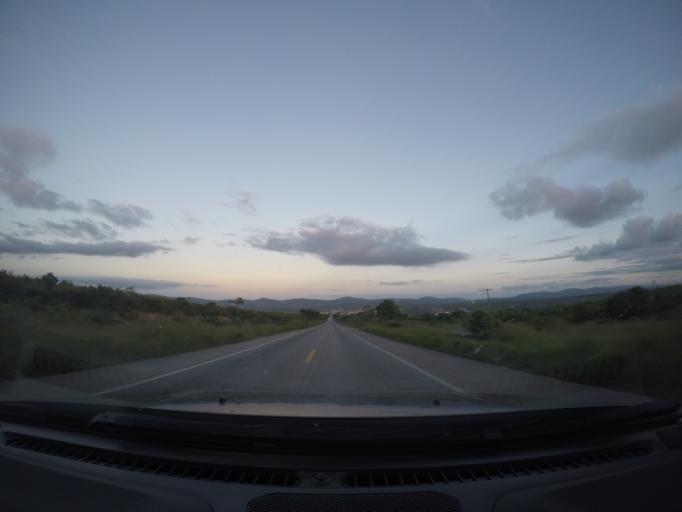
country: BR
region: Bahia
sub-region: Seabra
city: Seabra
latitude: -12.4316
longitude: -41.8018
